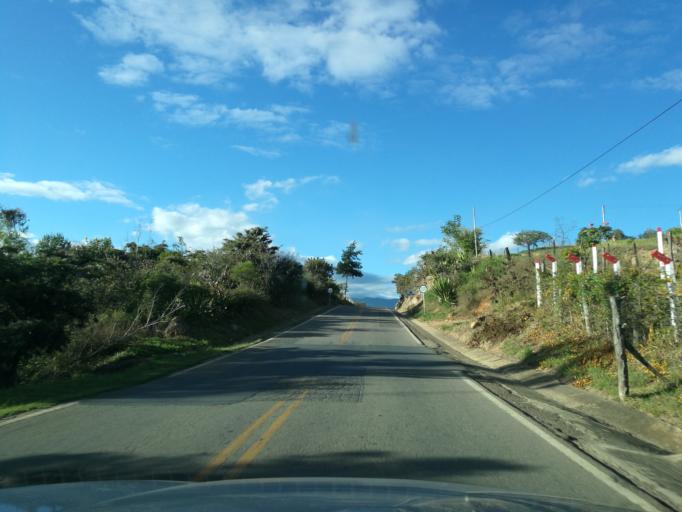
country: CO
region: Boyaca
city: Sutamarchan
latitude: 5.5978
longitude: -73.6384
